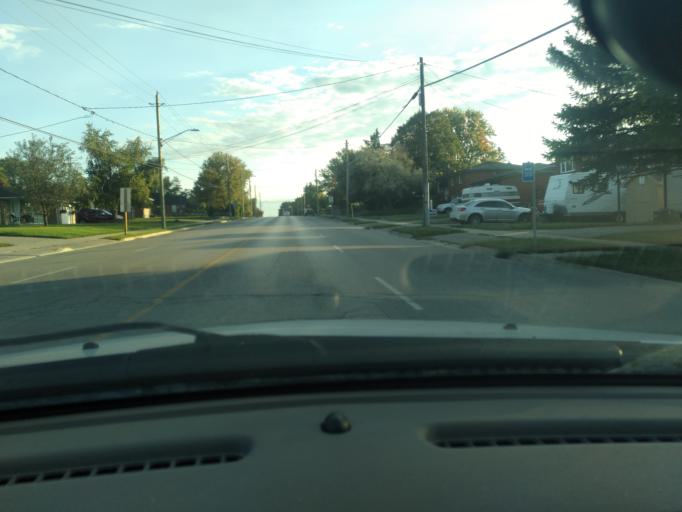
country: CA
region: Ontario
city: Bradford West Gwillimbury
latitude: 44.1046
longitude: -79.5672
